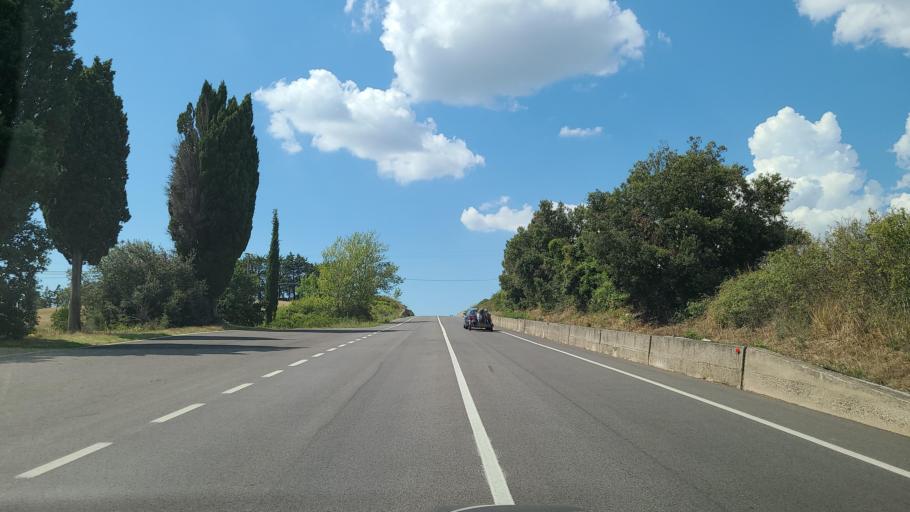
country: IT
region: Tuscany
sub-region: Provincia di Siena
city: San Gimignano
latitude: 43.4026
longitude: 10.9840
